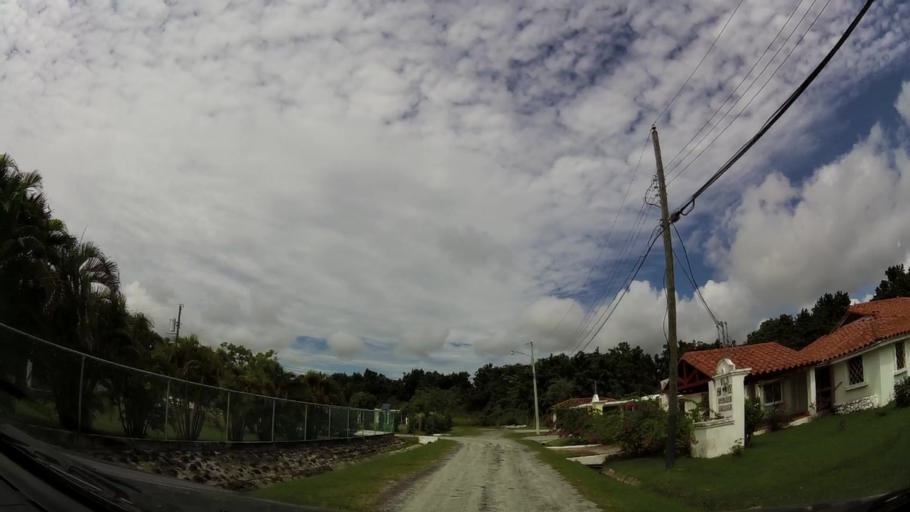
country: PA
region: Panama
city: Nueva Gorgona
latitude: 8.5419
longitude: -79.9077
